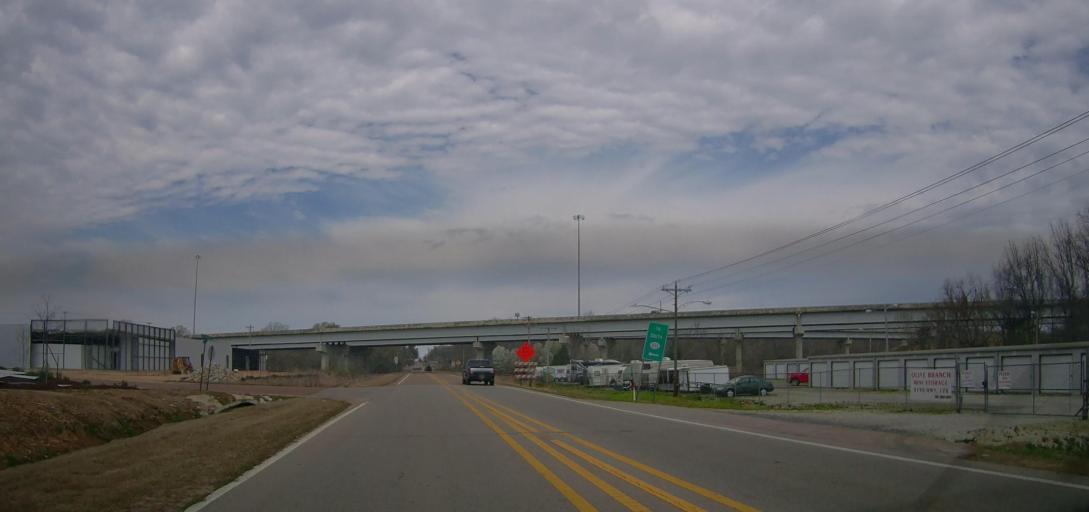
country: US
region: Mississippi
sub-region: De Soto County
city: Olive Branch
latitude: 34.9669
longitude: -89.8322
